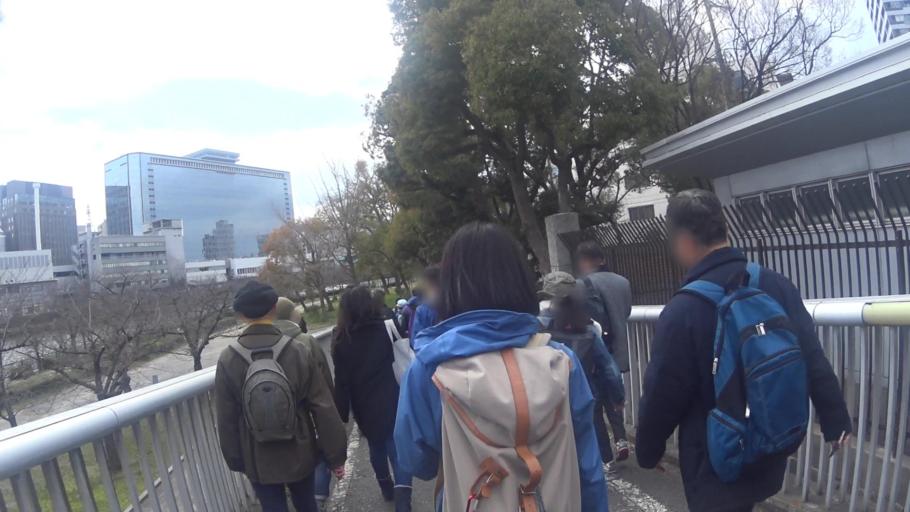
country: JP
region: Osaka
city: Osaka-shi
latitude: 34.6928
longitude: 135.5206
